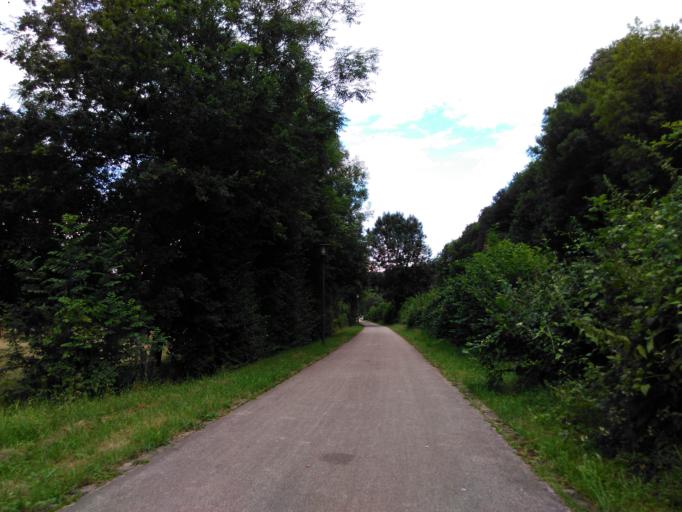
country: DE
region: Rheinland-Pfalz
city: Menningen
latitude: 49.8161
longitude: 6.4776
